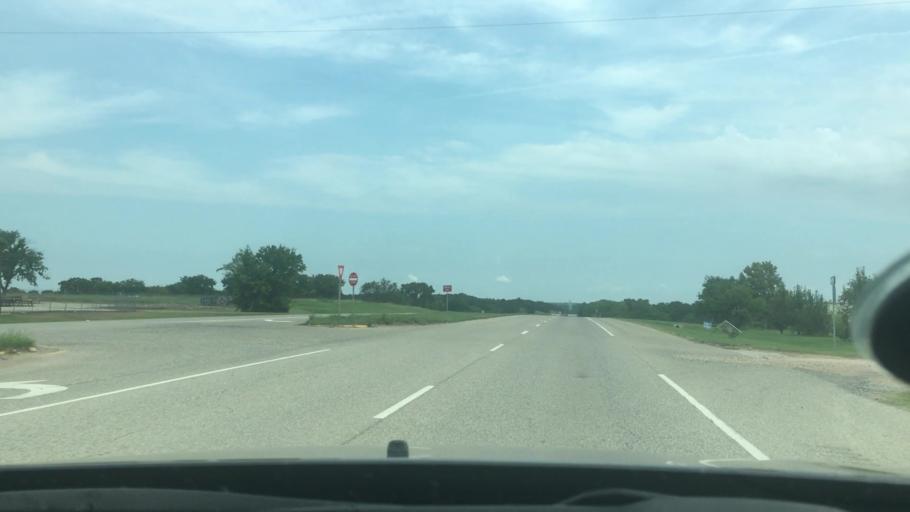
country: US
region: Oklahoma
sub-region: Seminole County
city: Seminole
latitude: 35.1955
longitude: -96.6749
